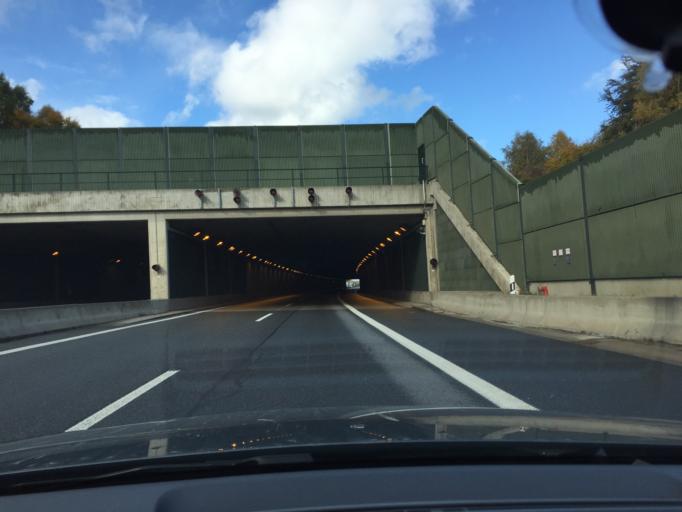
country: DE
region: Saxony
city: Liebstadt
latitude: 50.7853
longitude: 13.8953
